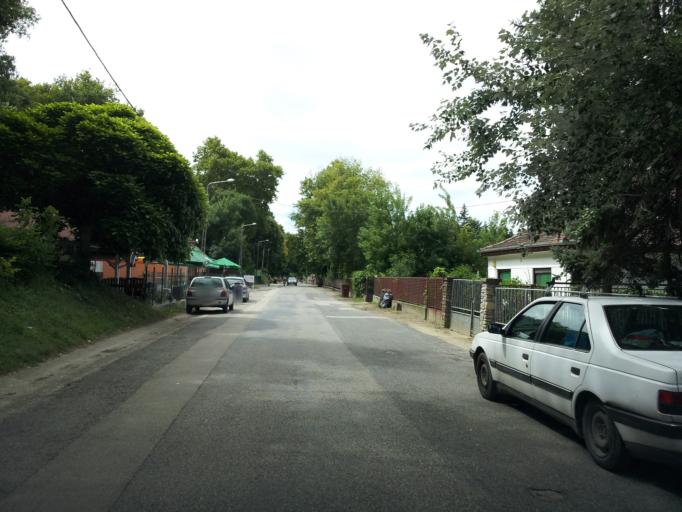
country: HU
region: Somogy
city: Balatonszabadi
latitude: 46.9667
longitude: 18.1587
